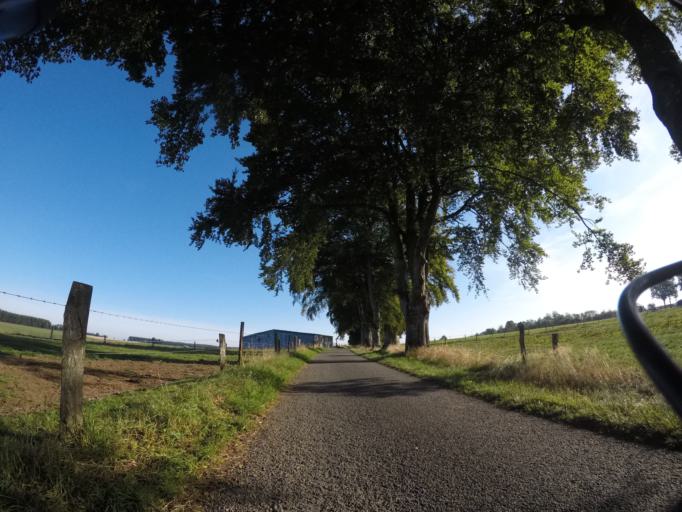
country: BE
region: Wallonia
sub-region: Province du Luxembourg
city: Bastogne
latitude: 49.9624
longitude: 5.7111
